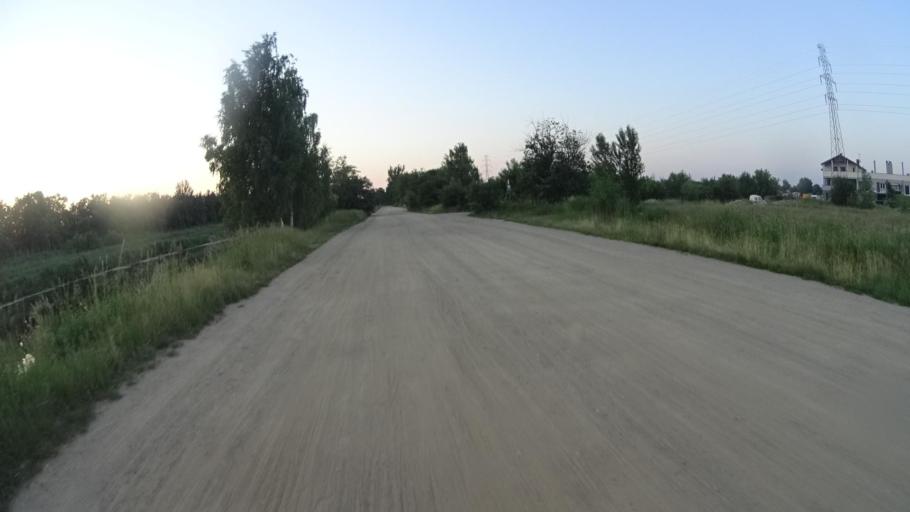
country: PL
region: Masovian Voivodeship
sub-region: Powiat legionowski
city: Stanislawow Pierwszy
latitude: 52.3453
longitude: 21.0339
